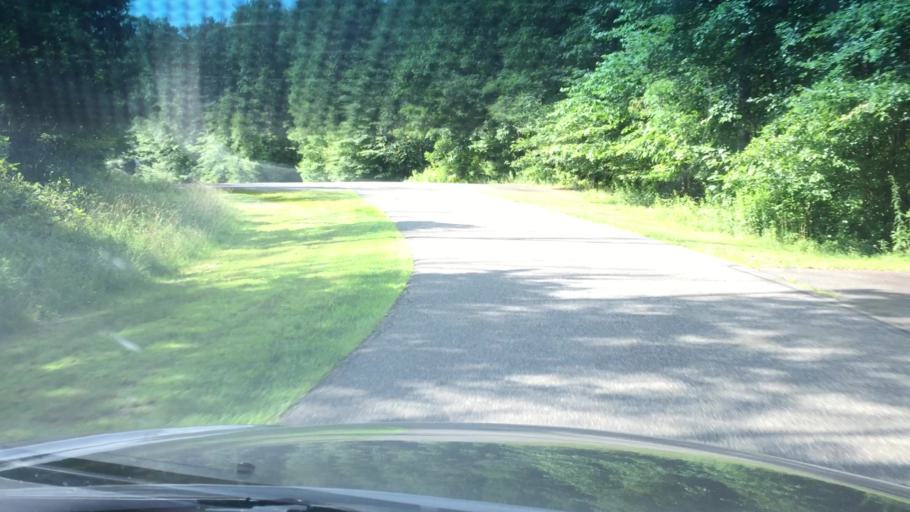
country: US
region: Pennsylvania
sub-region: Luzerne County
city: Harleigh
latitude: 41.0384
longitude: -75.9787
